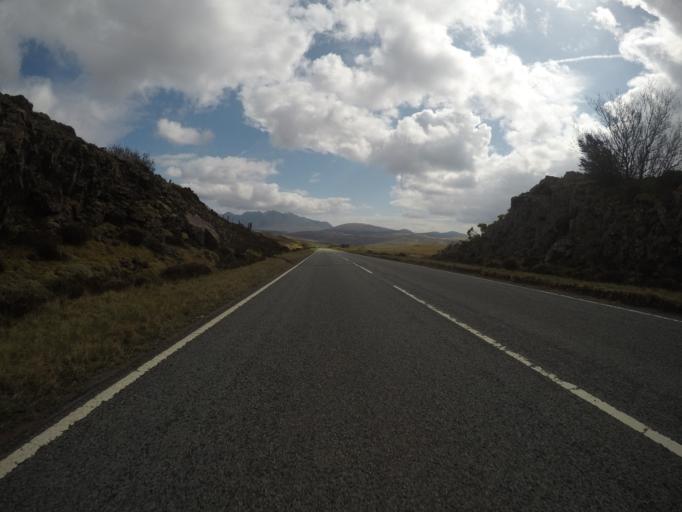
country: GB
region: Scotland
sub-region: Highland
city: Isle of Skye
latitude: 57.3114
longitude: -6.3189
